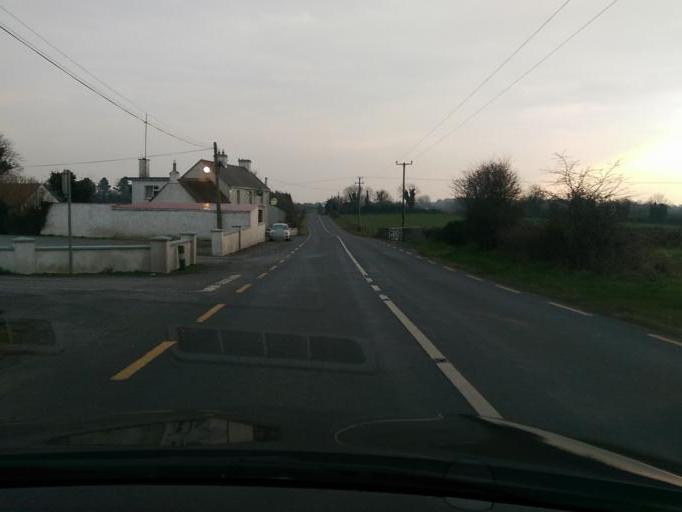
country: IE
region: Leinster
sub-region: An Longfort
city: Ballymahon
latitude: 53.5143
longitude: -7.8228
